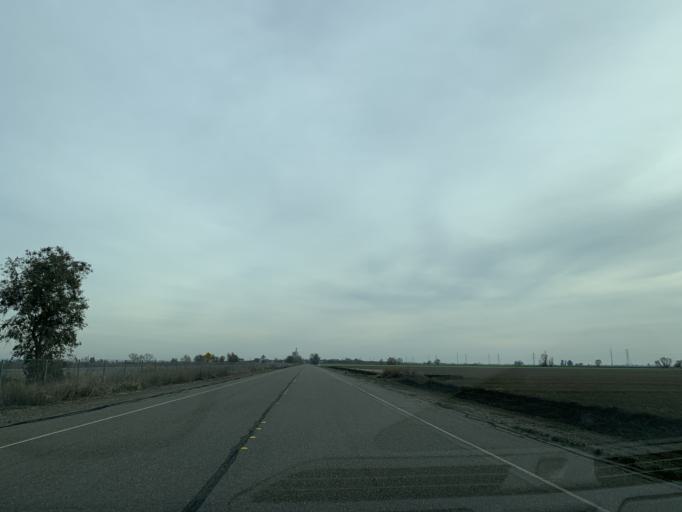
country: US
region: California
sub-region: Yuba County
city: Plumas Lake
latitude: 38.8628
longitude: -121.5524
